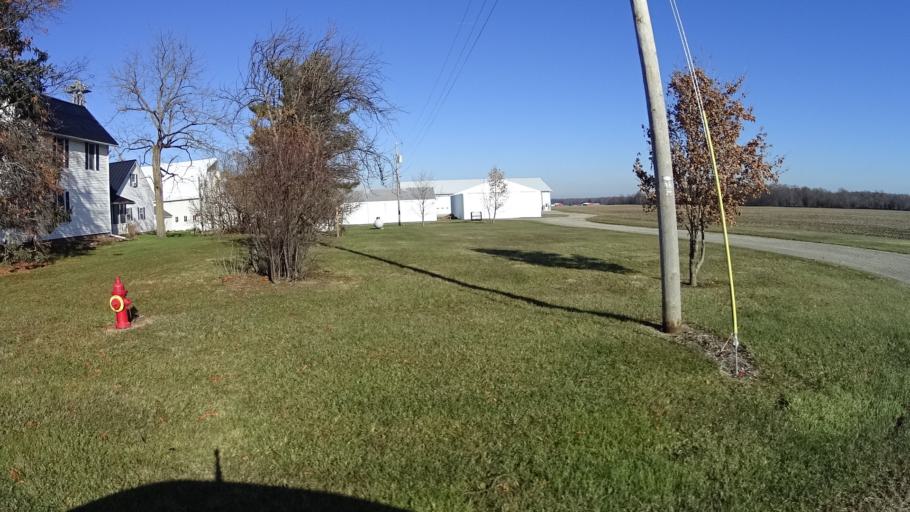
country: US
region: Ohio
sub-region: Huron County
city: New London
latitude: 41.0738
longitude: -82.2992
